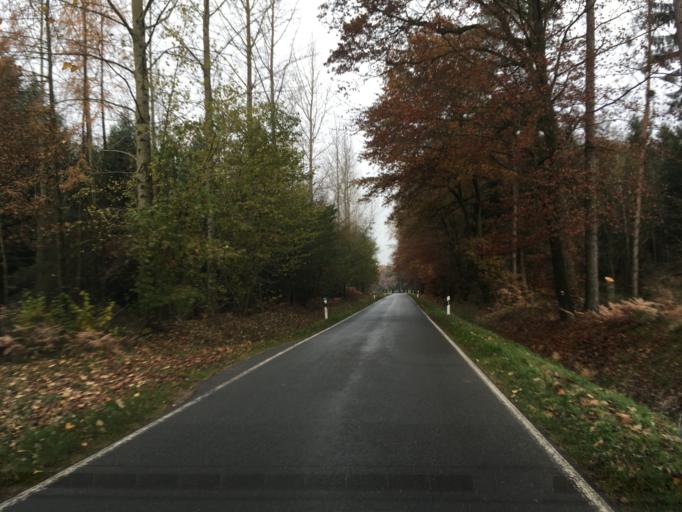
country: DE
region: North Rhine-Westphalia
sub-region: Regierungsbezirk Munster
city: Gescher
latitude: 52.0172
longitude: 6.9966
